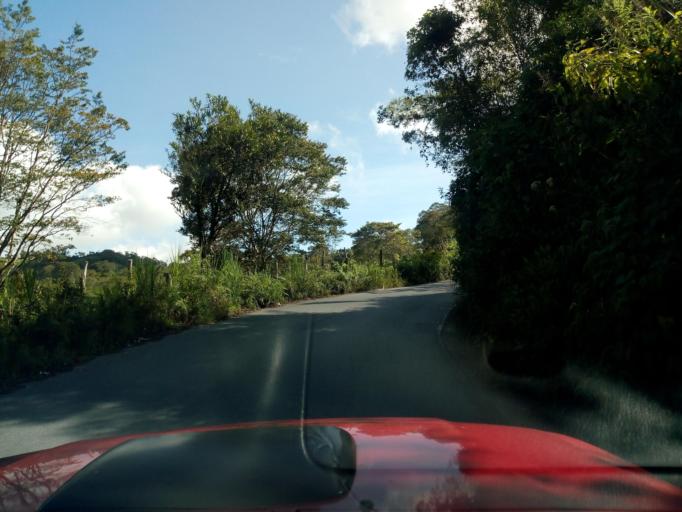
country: CO
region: Boyaca
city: Moniquira
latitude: 5.8783
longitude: -73.5492
